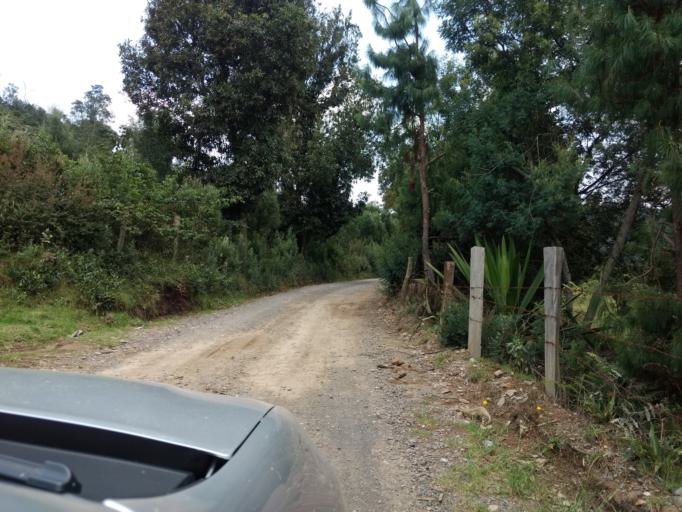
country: CO
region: Boyaca
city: Raquira
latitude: 5.5126
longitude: -73.7122
